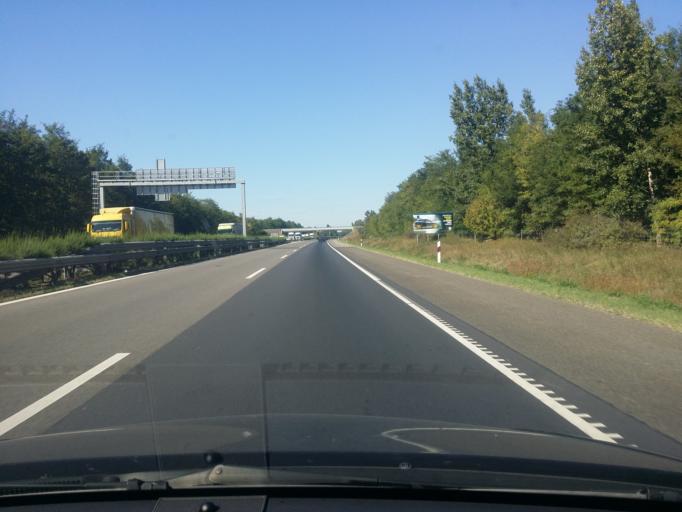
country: HU
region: Bacs-Kiskun
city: Helvecia
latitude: 46.8549
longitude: 19.6560
